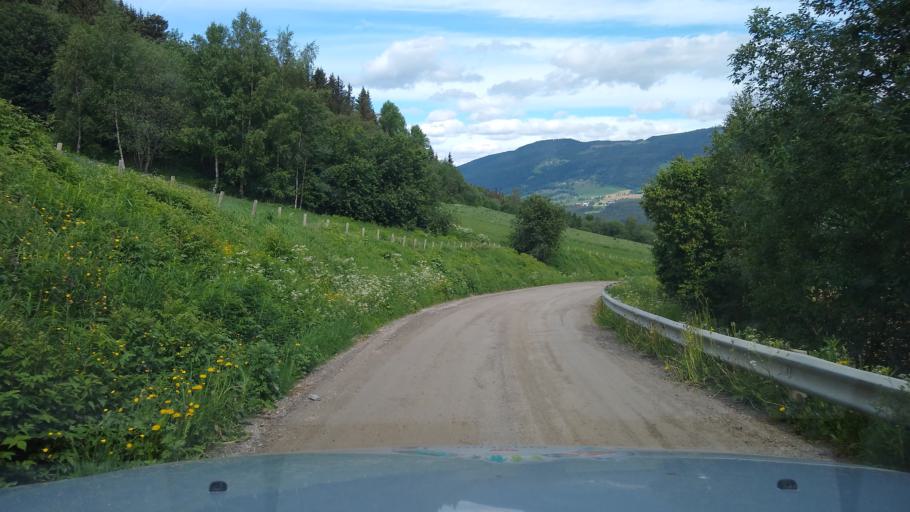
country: NO
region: Oppland
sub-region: Ringebu
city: Ringebu
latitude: 61.5126
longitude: 10.1333
